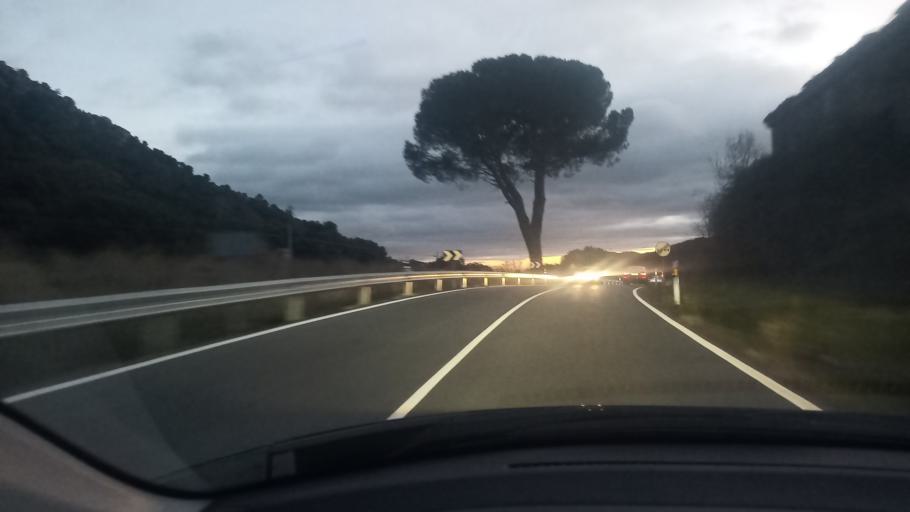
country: ES
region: Madrid
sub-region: Provincia de Madrid
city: Robledo de Chavela
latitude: 40.4509
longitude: -4.2625
